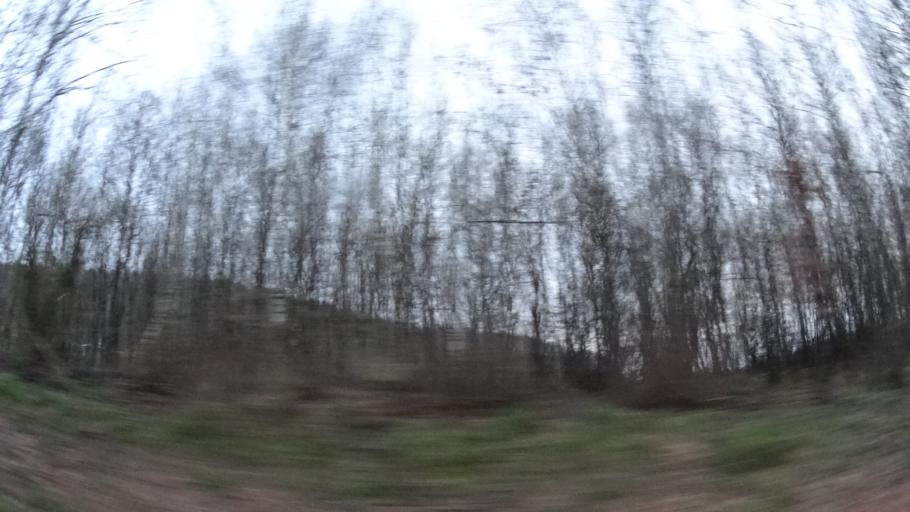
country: DE
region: Rheinland-Pfalz
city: Brucken
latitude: 49.6232
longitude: 7.1246
